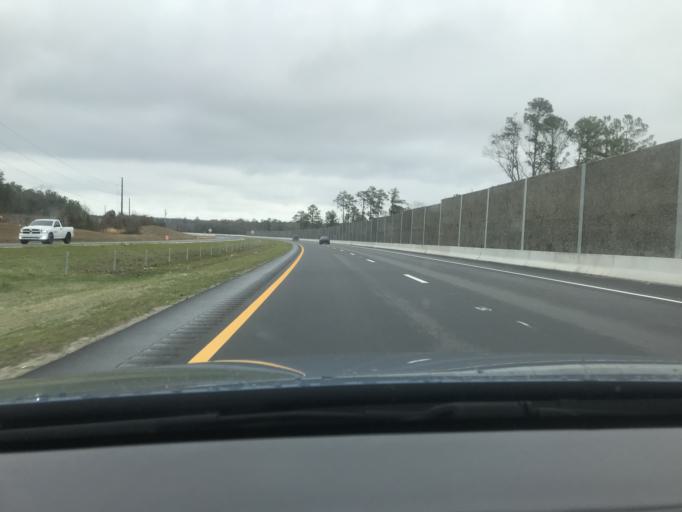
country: US
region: North Carolina
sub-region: Cumberland County
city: Fort Bragg
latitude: 35.0749
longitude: -79.0205
